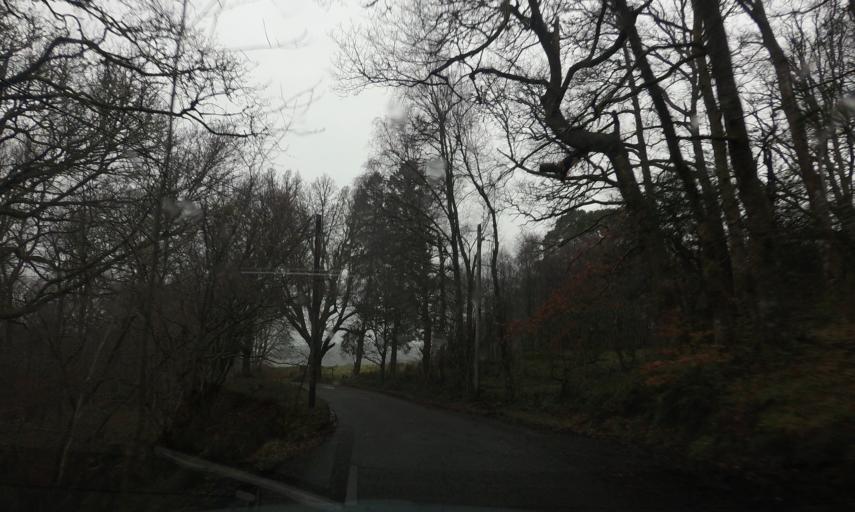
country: GB
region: Scotland
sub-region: West Dunbartonshire
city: Balloch
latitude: 56.1358
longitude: -4.6130
